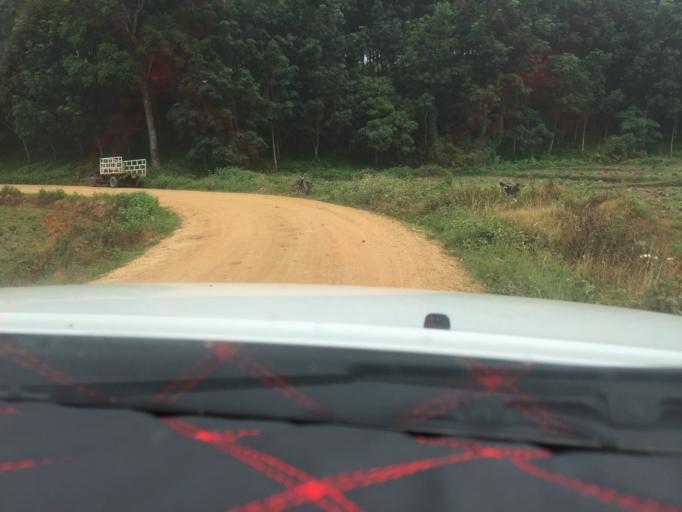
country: TH
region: Phayao
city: Phu Sang
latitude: 19.6950
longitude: 100.5004
